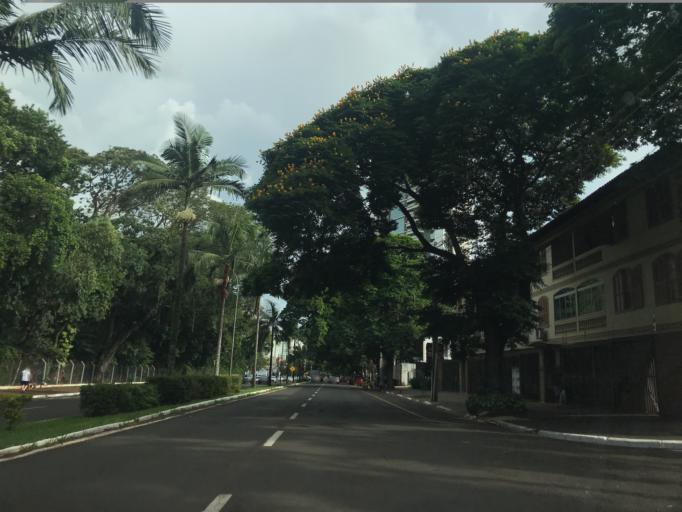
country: BR
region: Parana
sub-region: Maringa
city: Maringa
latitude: -23.4320
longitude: -51.9299
